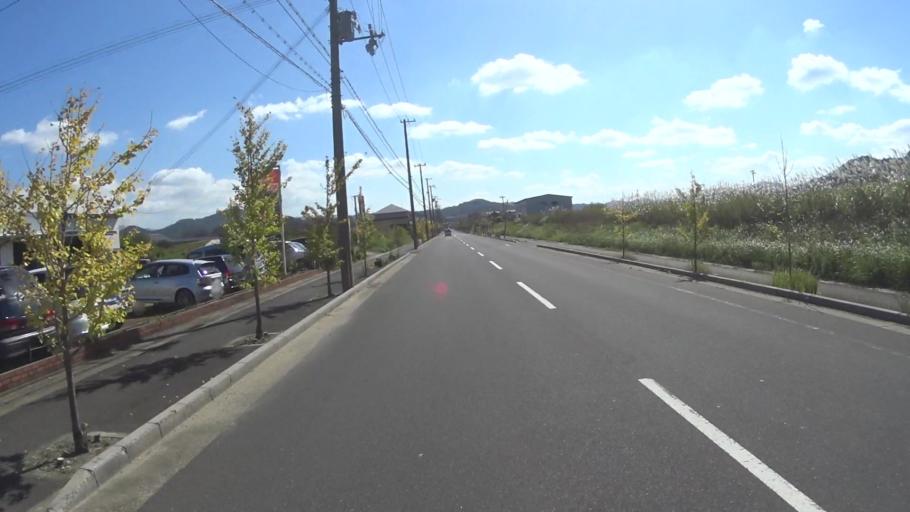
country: JP
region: Kyoto
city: Miyazu
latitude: 35.6826
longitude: 135.0196
